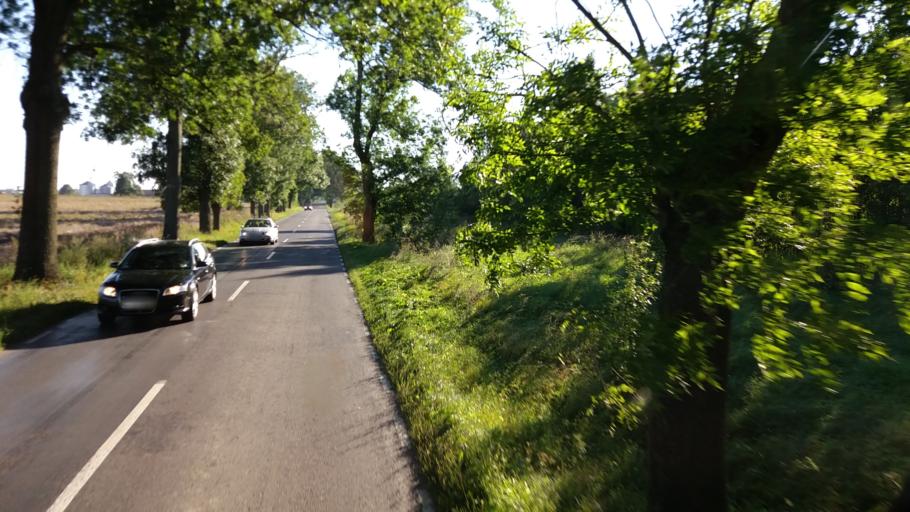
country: PL
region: West Pomeranian Voivodeship
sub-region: Powiat choszczenski
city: Choszczno
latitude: 53.1879
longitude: 15.4315
